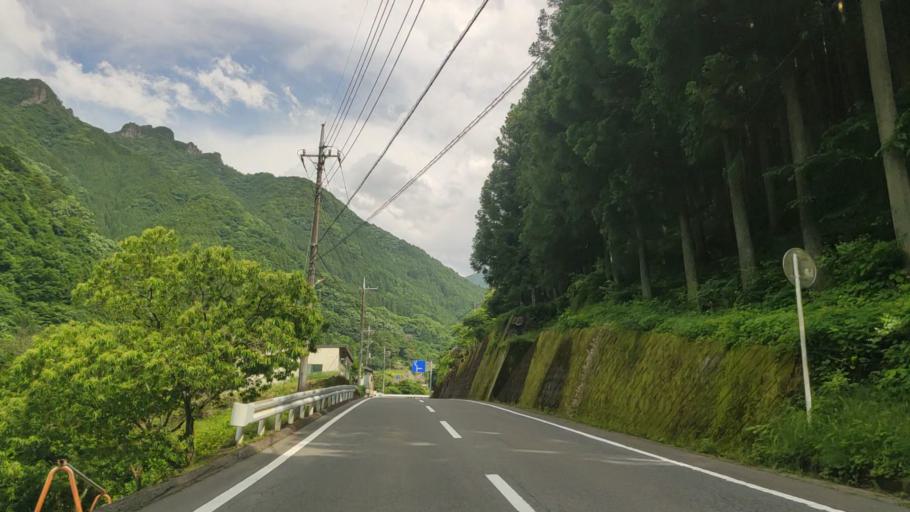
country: JP
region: Gunma
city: Tomioka
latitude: 36.1485
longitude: 138.7331
